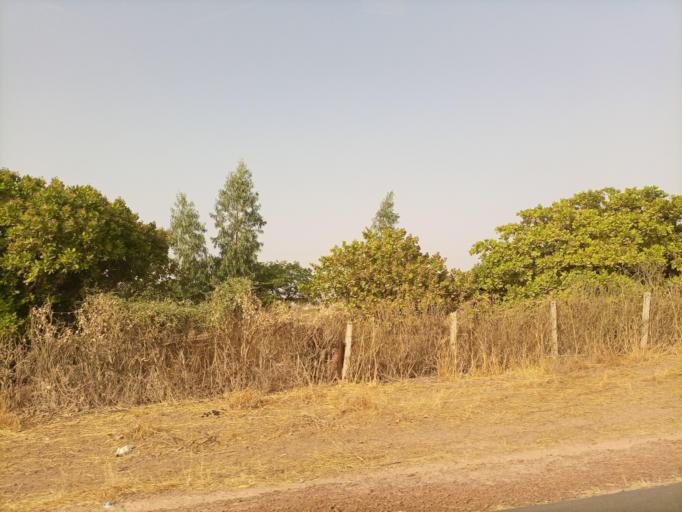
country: SN
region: Fatick
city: Passi
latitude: 14.0309
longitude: -16.3103
